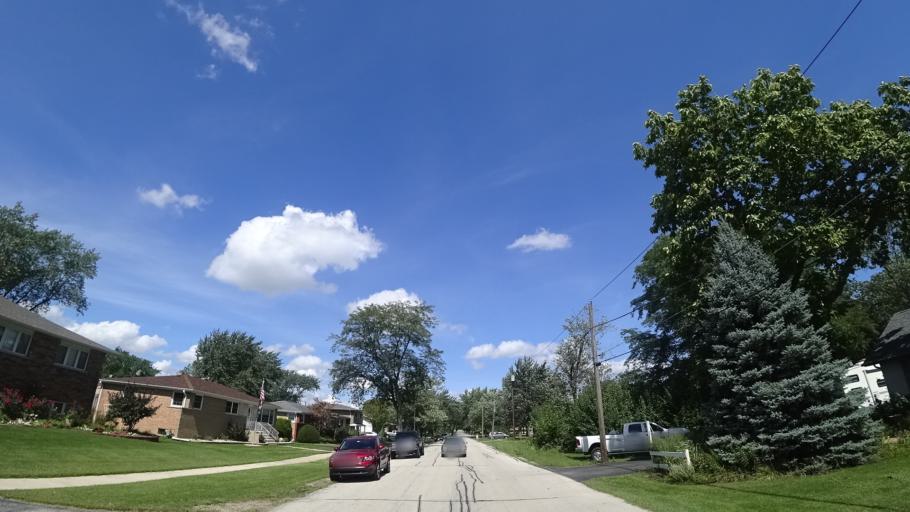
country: US
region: Illinois
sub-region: Cook County
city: Tinley Park
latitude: 41.5683
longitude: -87.7886
